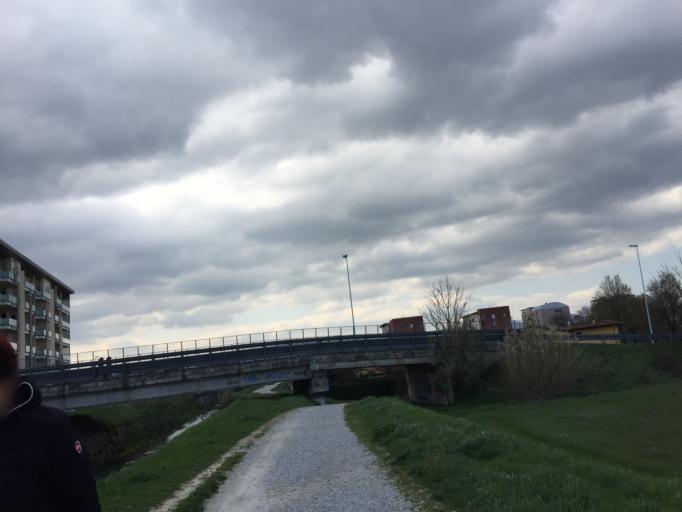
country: IT
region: Tuscany
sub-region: Provincia di Prato
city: Fornacelle
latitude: 43.8913
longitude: 11.0563
